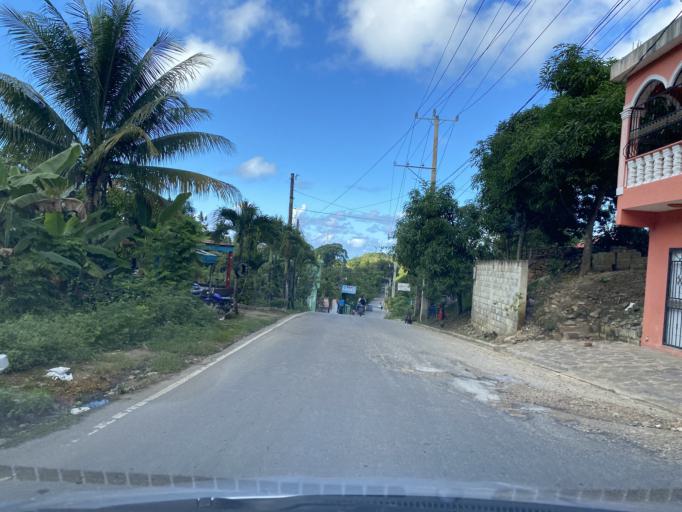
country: DO
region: Samana
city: Las Terrenas
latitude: 19.2875
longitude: -69.5479
